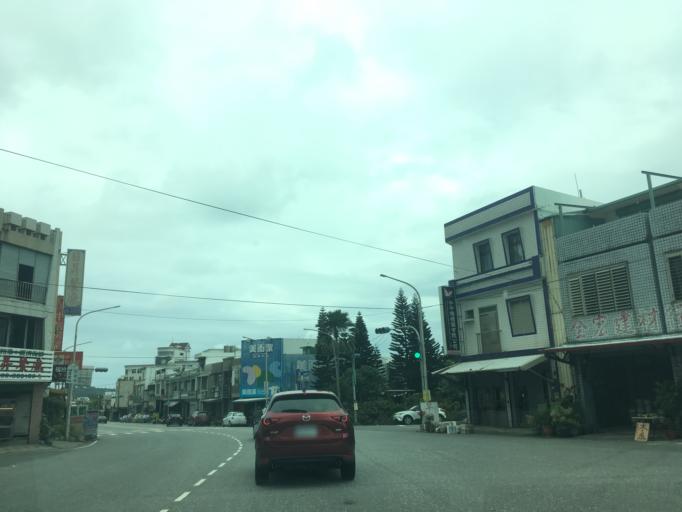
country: TW
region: Taiwan
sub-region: Taitung
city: Taitung
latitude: 23.1040
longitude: 121.3787
